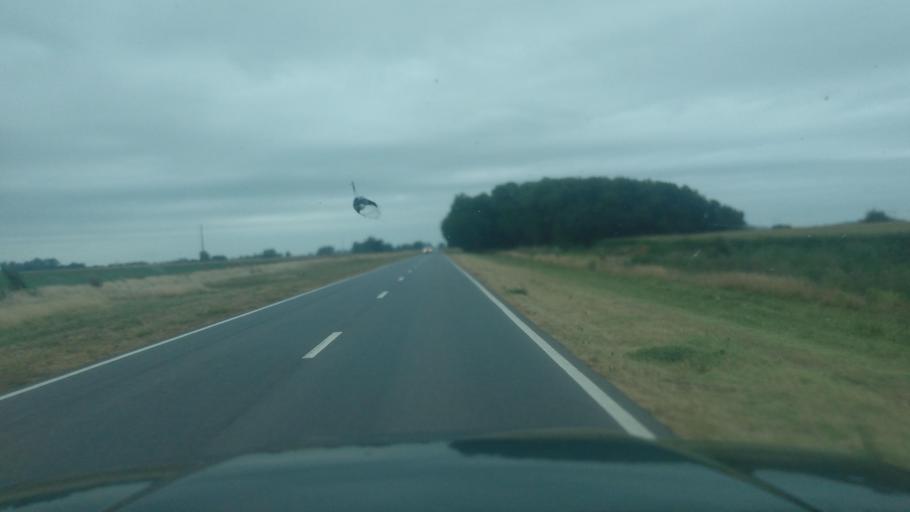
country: AR
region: Buenos Aires
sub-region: Partido de Bragado
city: Bragado
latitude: -35.2969
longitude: -60.6099
